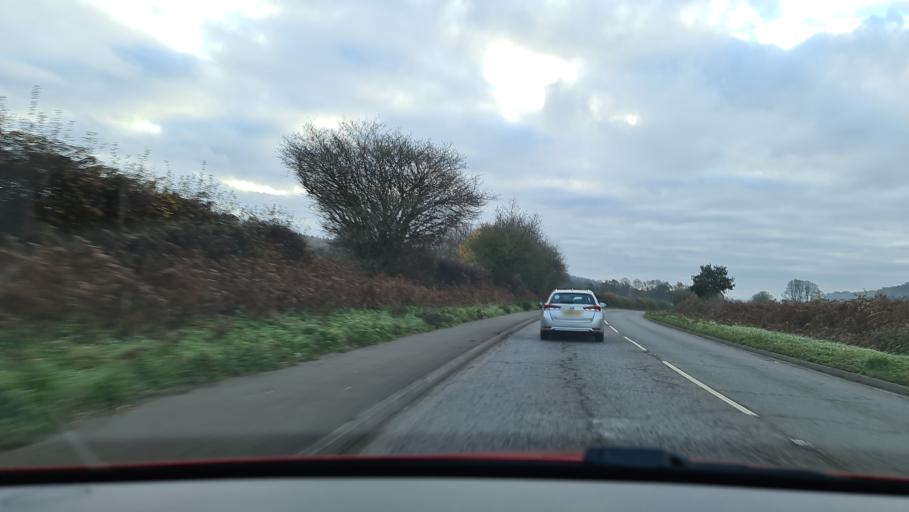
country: GB
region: England
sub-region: Buckinghamshire
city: Princes Risborough
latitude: 51.6702
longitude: -0.8141
